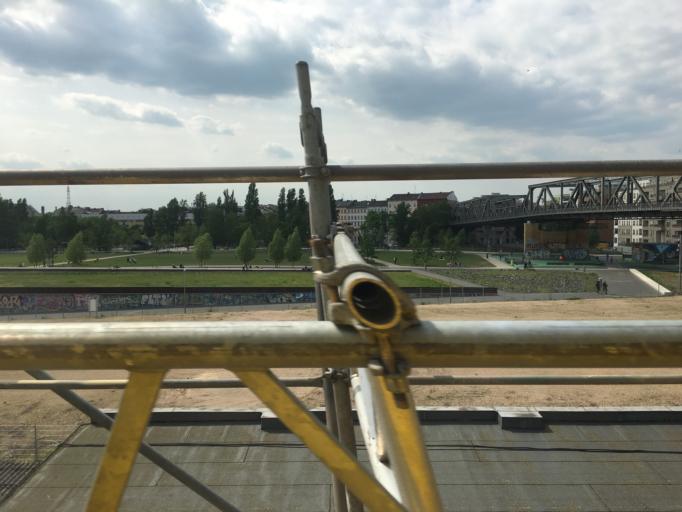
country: DE
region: Berlin
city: Tiergarten Bezirk
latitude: 52.4989
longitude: 13.3738
